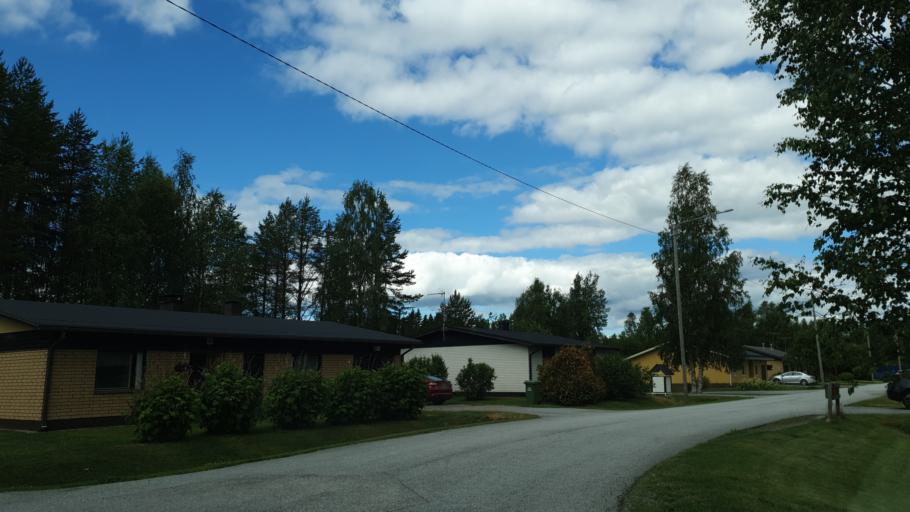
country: FI
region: Kainuu
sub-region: Kehys-Kainuu
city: Kuhmo
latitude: 64.1142
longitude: 29.4804
